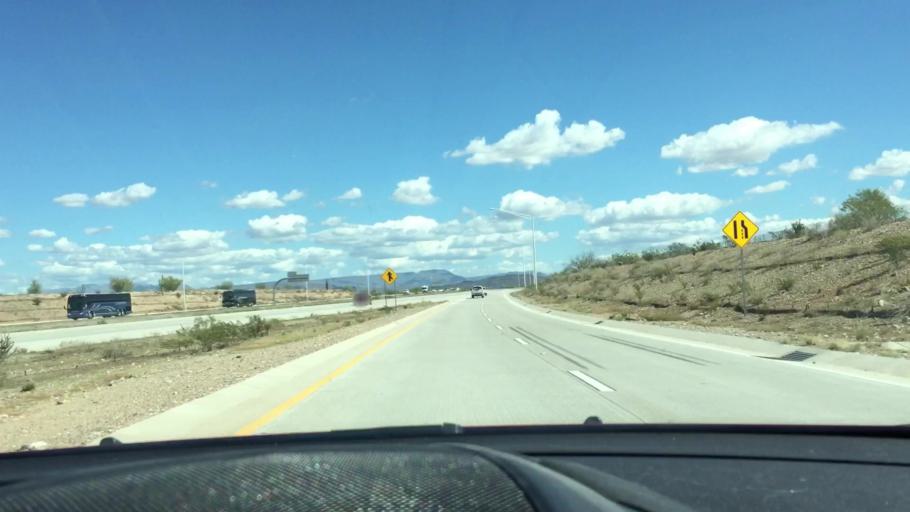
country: US
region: Arizona
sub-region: Maricopa County
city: Anthem
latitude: 33.7707
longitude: -112.2466
